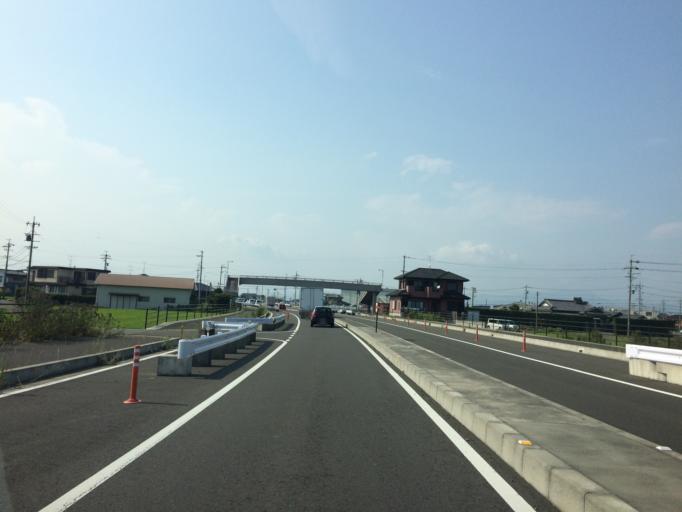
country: JP
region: Shizuoka
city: Yaizu
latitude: 34.8161
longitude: 138.3109
